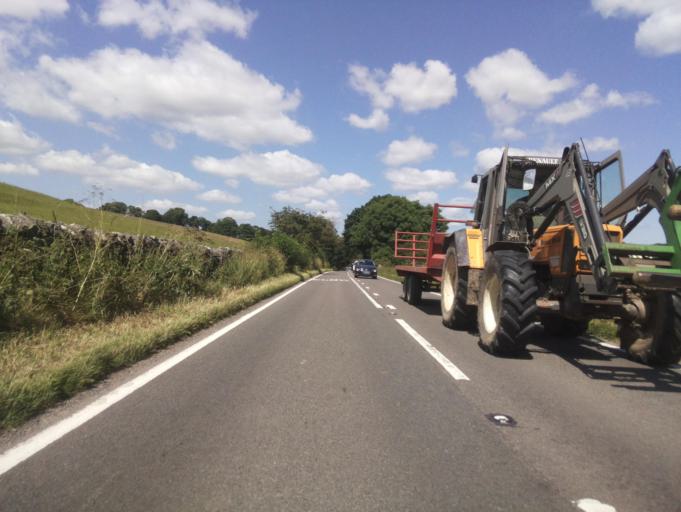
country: GB
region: England
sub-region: Derbyshire
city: Ashbourne
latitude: 53.0808
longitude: -1.7598
